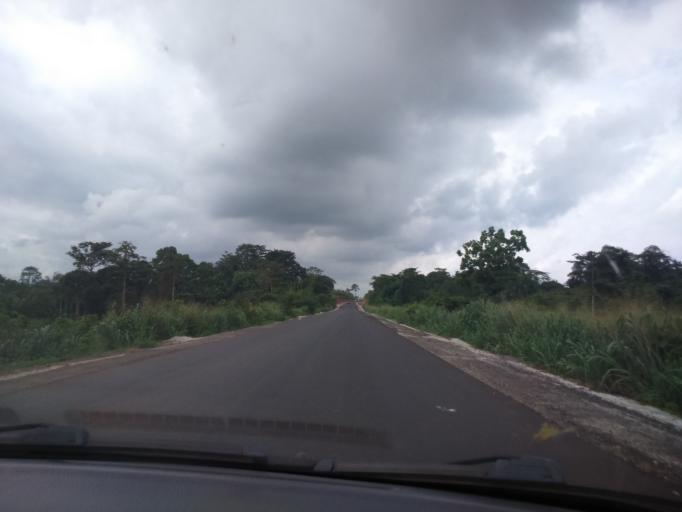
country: CI
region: Lagunes
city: Akoupe
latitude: 6.5001
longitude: -3.8272
